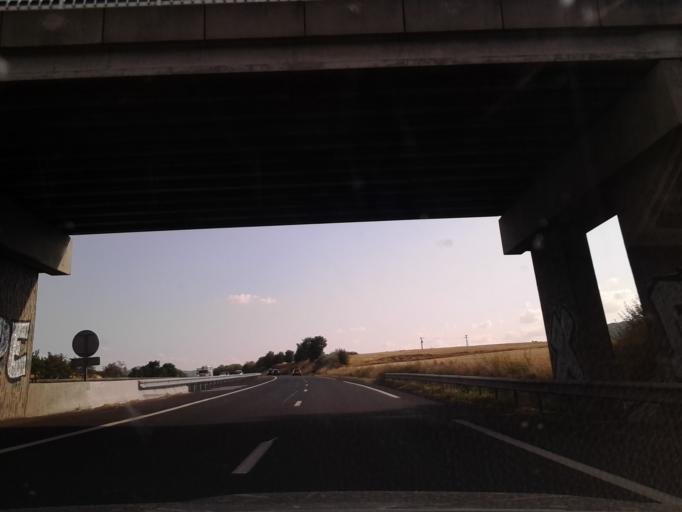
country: FR
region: Auvergne
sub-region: Departement du Puy-de-Dome
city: Le Breuil-sur-Couze
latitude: 45.4913
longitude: 3.2488
